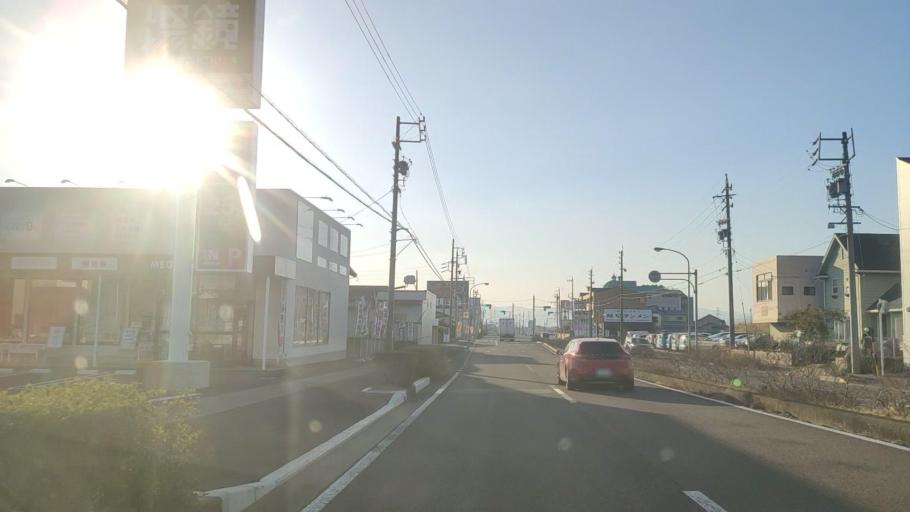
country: JP
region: Gifu
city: Gifu-shi
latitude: 35.4541
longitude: 136.7568
